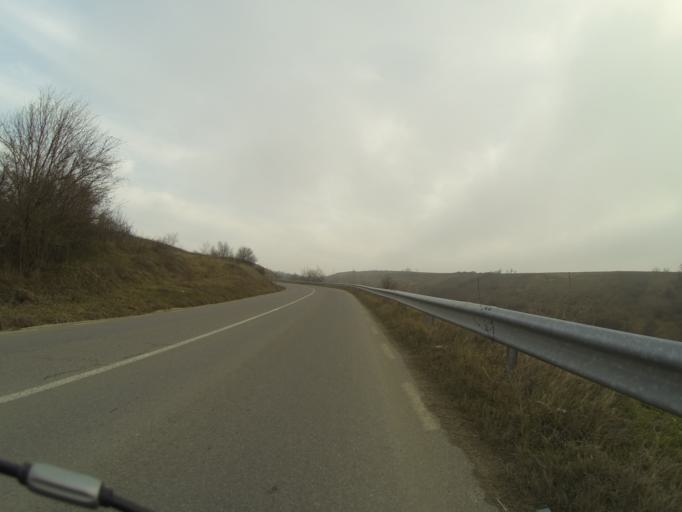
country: RO
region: Mehedinti
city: Vanju-Mare
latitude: 44.4130
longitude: 22.8775
